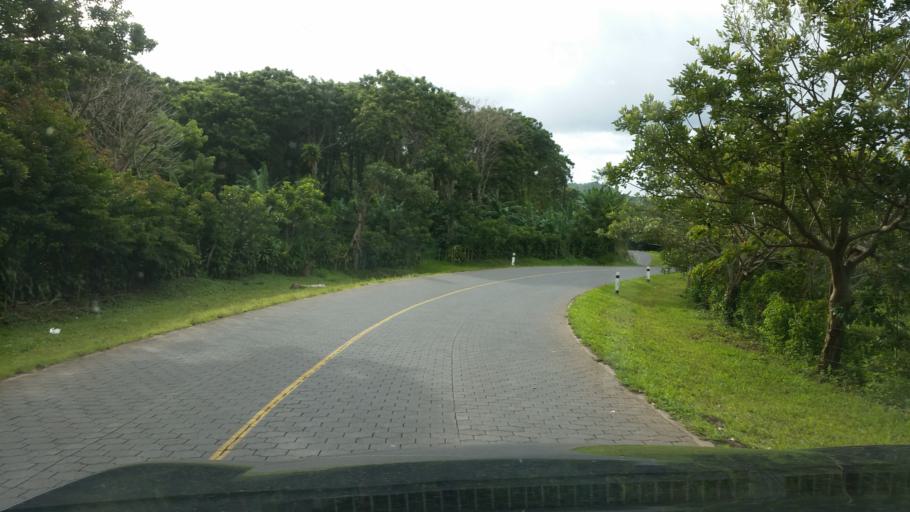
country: NI
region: Matagalpa
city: San Ramon
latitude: 13.1759
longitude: -85.7303
